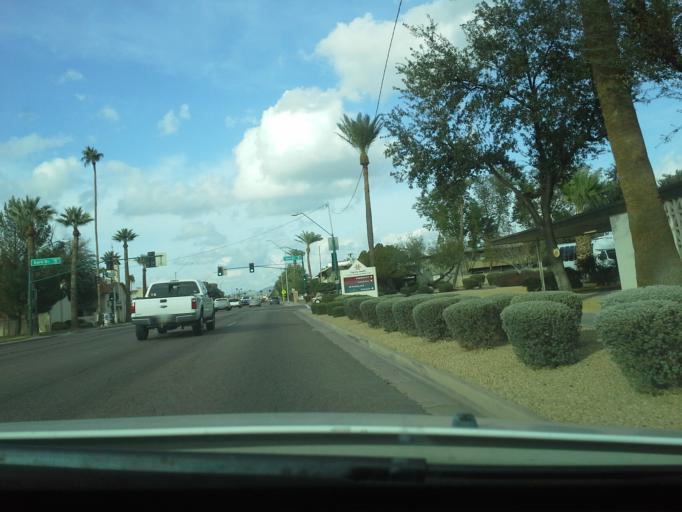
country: US
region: Arizona
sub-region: Maricopa County
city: Phoenix
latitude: 33.4828
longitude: -112.0830
